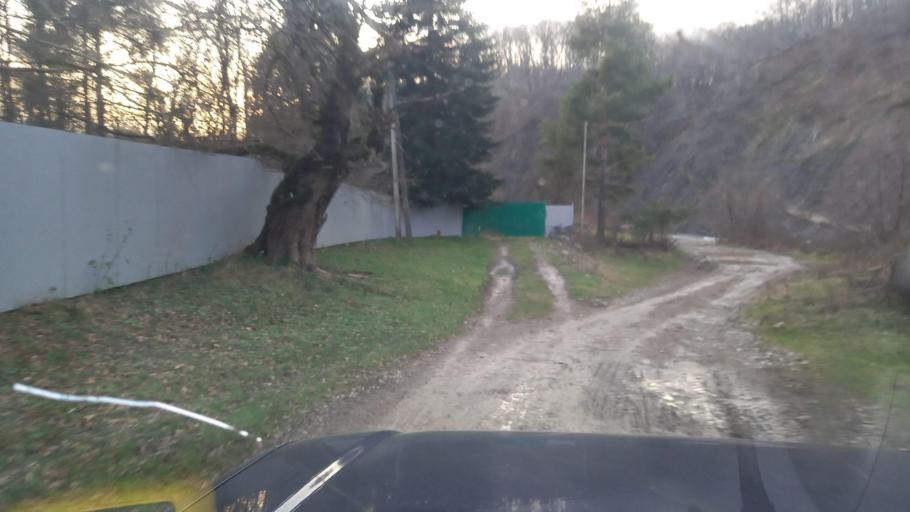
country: RU
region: Krasnodarskiy
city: Goryachiy Klyuch
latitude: 44.3862
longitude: 39.1638
